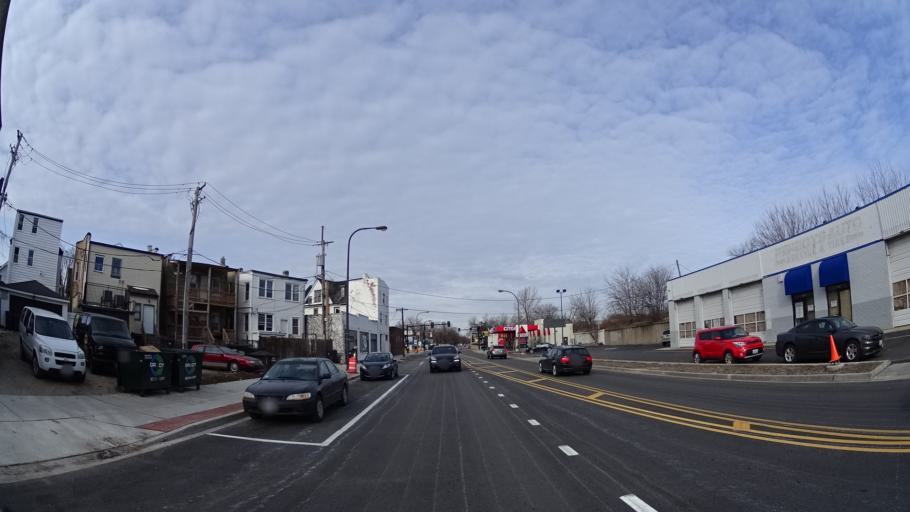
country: US
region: Illinois
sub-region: Cook County
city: Evanston
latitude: 42.0526
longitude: -87.6892
